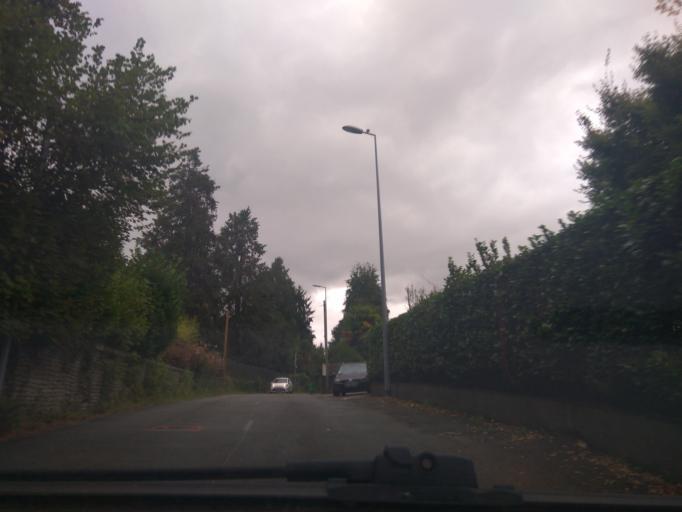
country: FR
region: Aquitaine
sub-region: Departement des Pyrenees-Atlantiques
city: Bizanos
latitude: 43.2971
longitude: -0.3350
